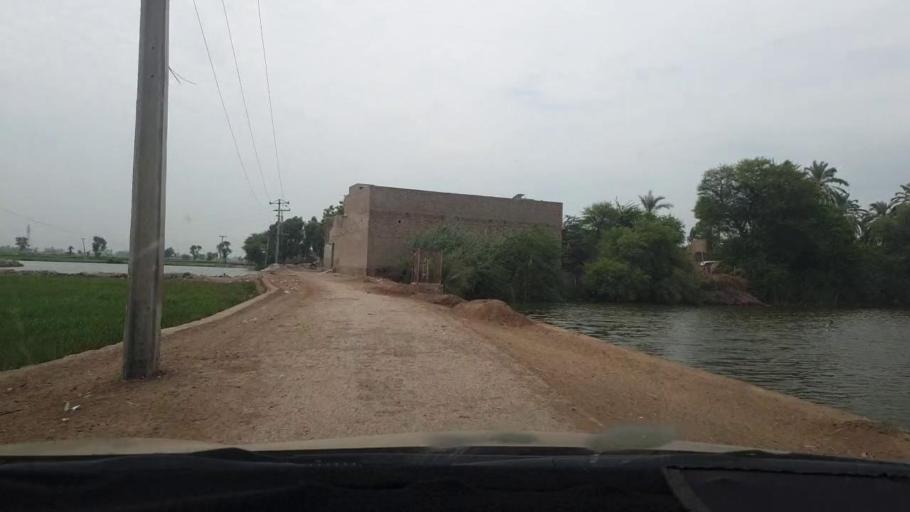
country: PK
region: Sindh
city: Naudero
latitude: 27.6777
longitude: 68.3346
